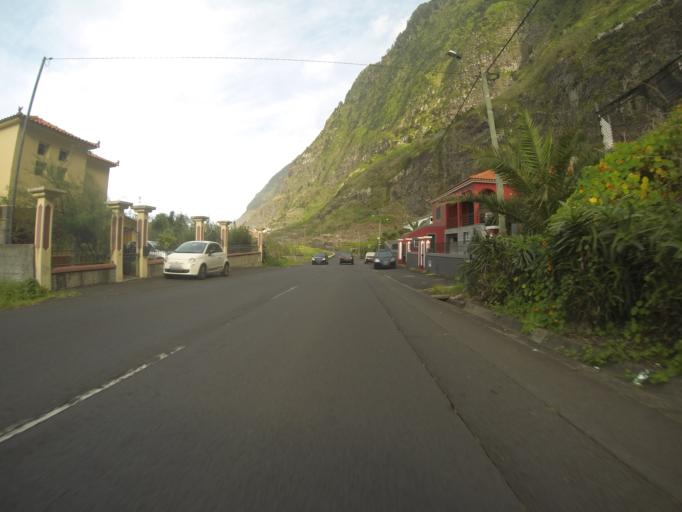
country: PT
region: Madeira
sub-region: Sao Vicente
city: Sao Vicente
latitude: 32.8111
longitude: -17.0403
